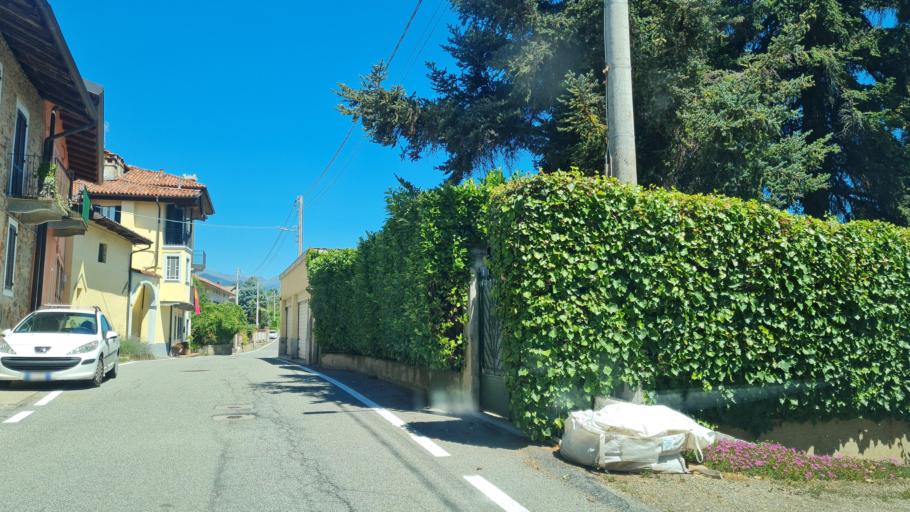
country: IT
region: Piedmont
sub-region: Provincia di Biella
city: Lessona
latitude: 45.5902
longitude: 8.2011
